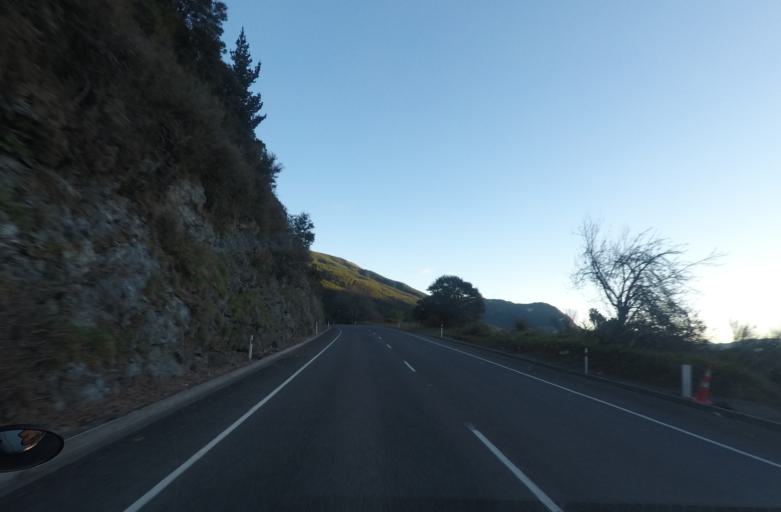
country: NZ
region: Marlborough
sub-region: Marlborough District
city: Picton
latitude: -41.2775
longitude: 173.7293
